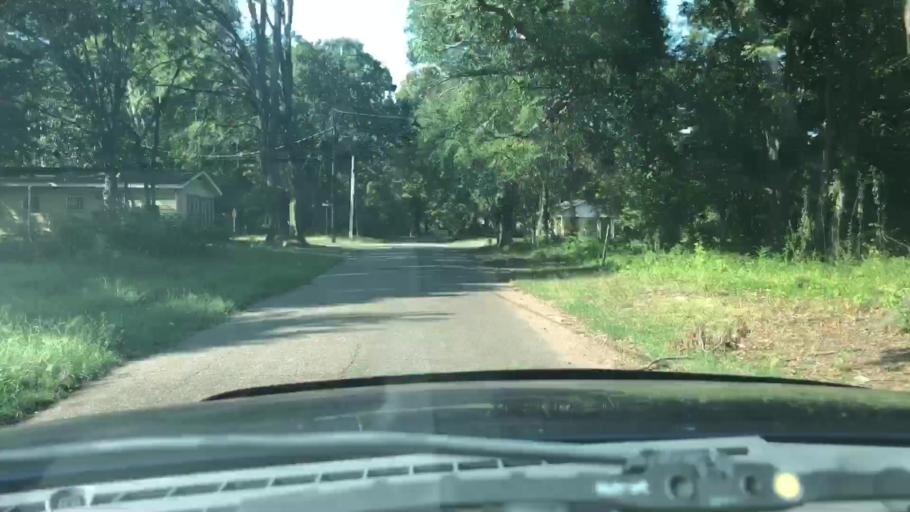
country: US
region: Texas
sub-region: Bowie County
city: Texarkana
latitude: 33.4151
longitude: -94.0628
